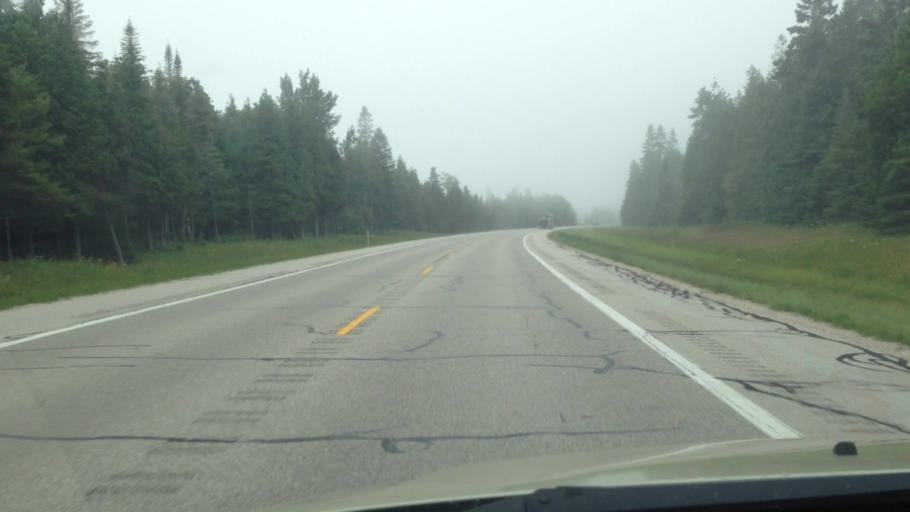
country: US
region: Michigan
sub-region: Luce County
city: Newberry
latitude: 46.1000
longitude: -85.4353
